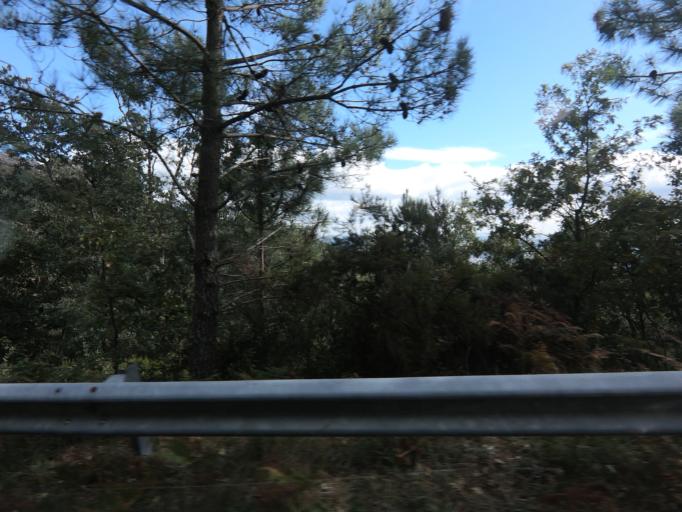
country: PT
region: Vila Real
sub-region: Vila Real
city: Vila Real
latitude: 41.3382
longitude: -7.7815
